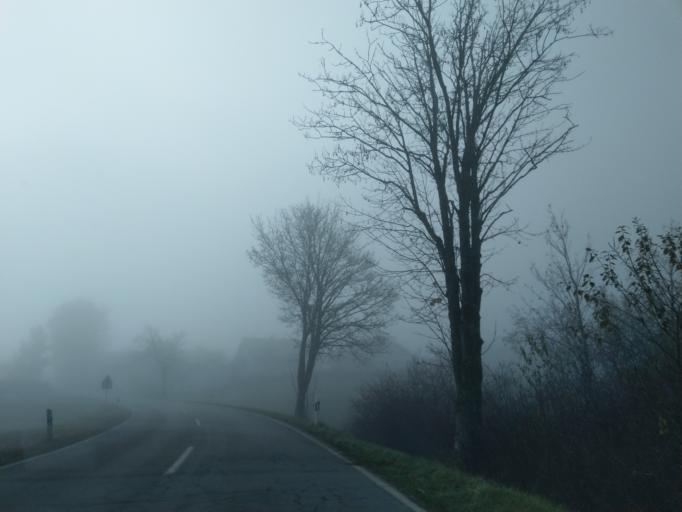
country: DE
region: Bavaria
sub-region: Lower Bavaria
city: Aussernzell
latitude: 48.7271
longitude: 13.2041
